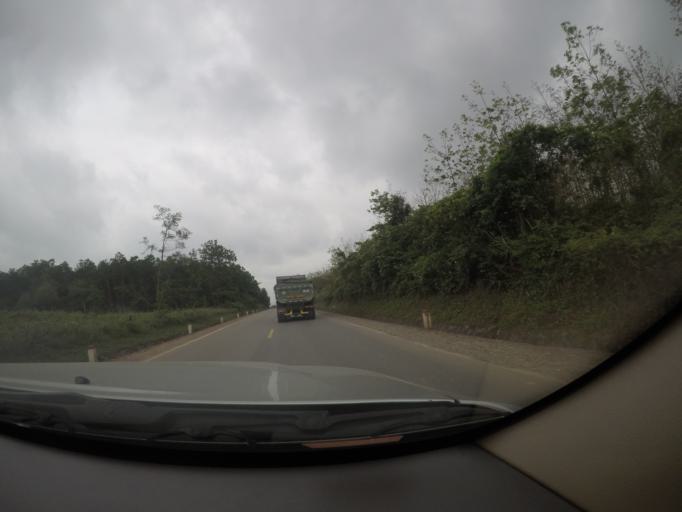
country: VN
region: Quang Binh
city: Kien Giang
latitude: 17.1563
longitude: 106.7473
